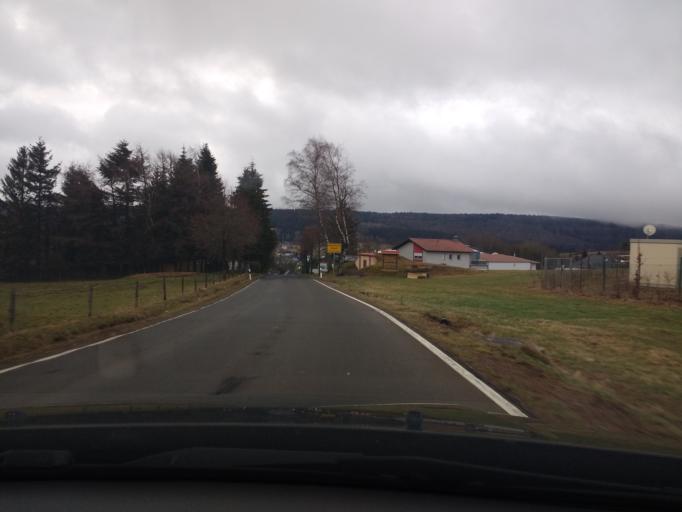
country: DE
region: Rheinland-Pfalz
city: Zusch
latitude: 49.6511
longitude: 7.0009
